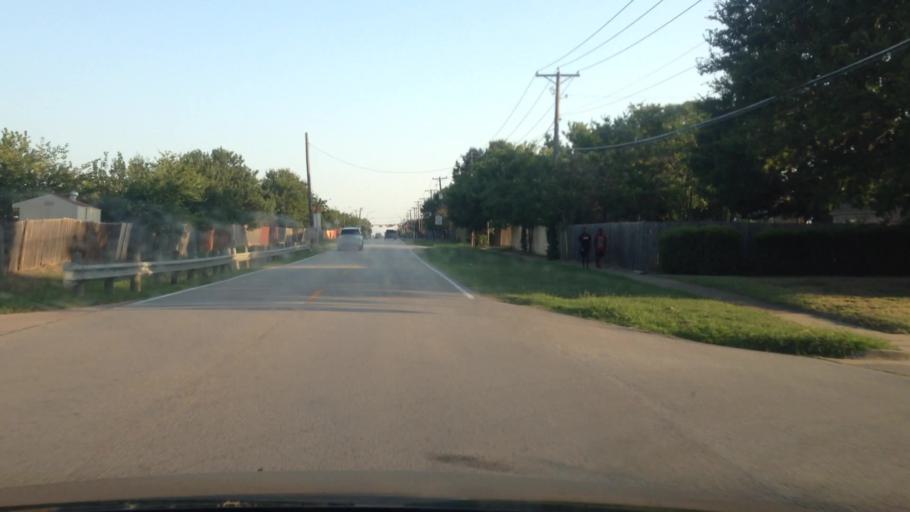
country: US
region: Texas
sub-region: Tarrant County
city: Dalworthington Gardens
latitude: 32.6485
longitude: -97.1023
